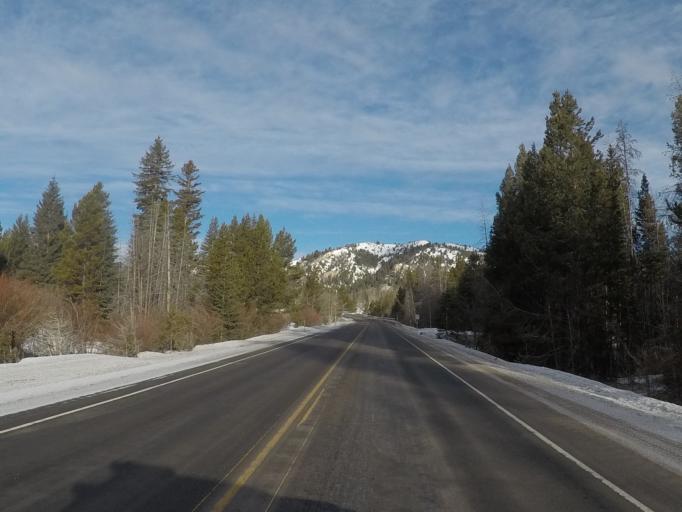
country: US
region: Montana
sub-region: Deer Lodge County
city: Anaconda
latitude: 46.1664
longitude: -113.1538
